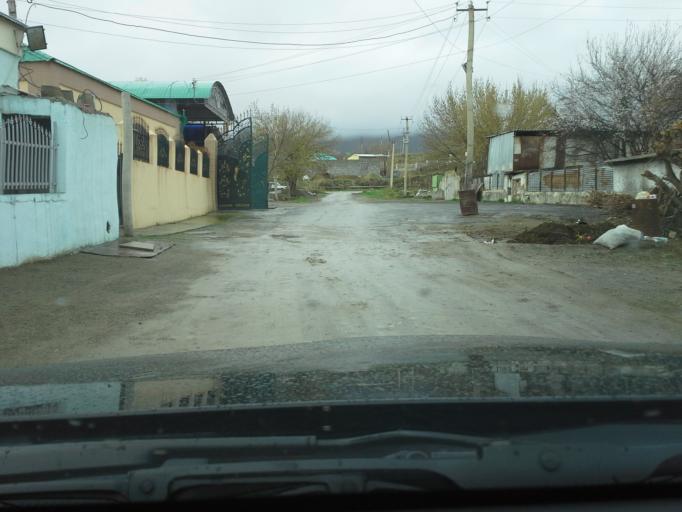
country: TM
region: Ahal
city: Abadan
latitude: 37.9617
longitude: 58.2129
